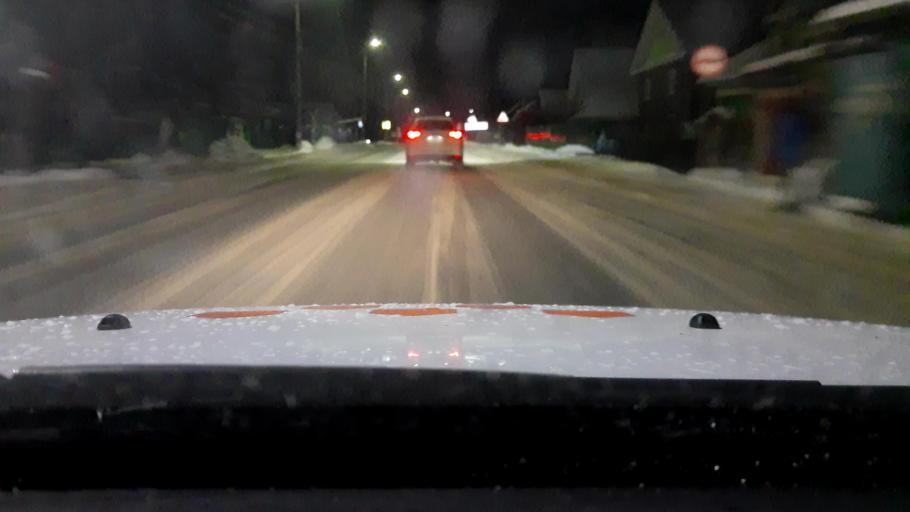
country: RU
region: Nizjnij Novgorod
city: Gorodets
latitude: 56.6576
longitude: 43.4781
